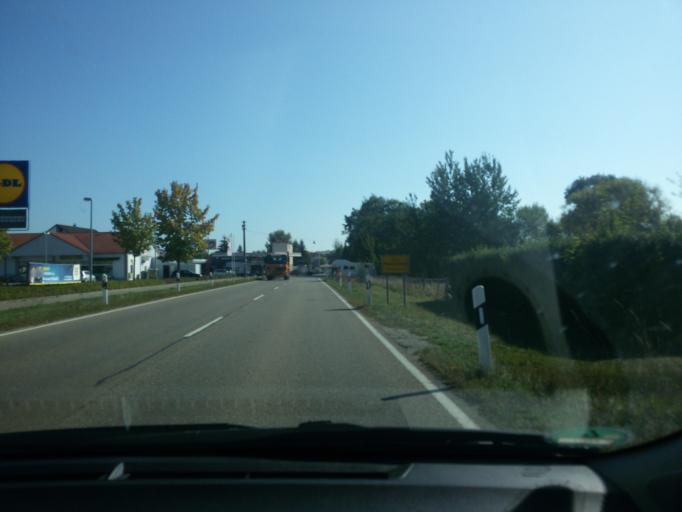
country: DE
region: Bavaria
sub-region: Regierungsbezirk Mittelfranken
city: Wassertrudingen
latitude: 49.0418
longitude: 10.5886
